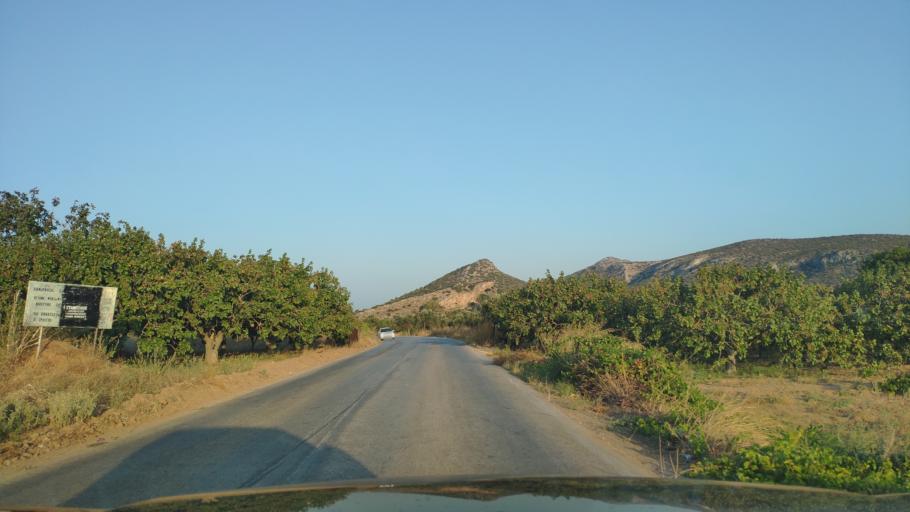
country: GR
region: Attica
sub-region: Nomarchia Anatolikis Attikis
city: Limin Mesoyaias
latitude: 37.9263
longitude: 23.9859
